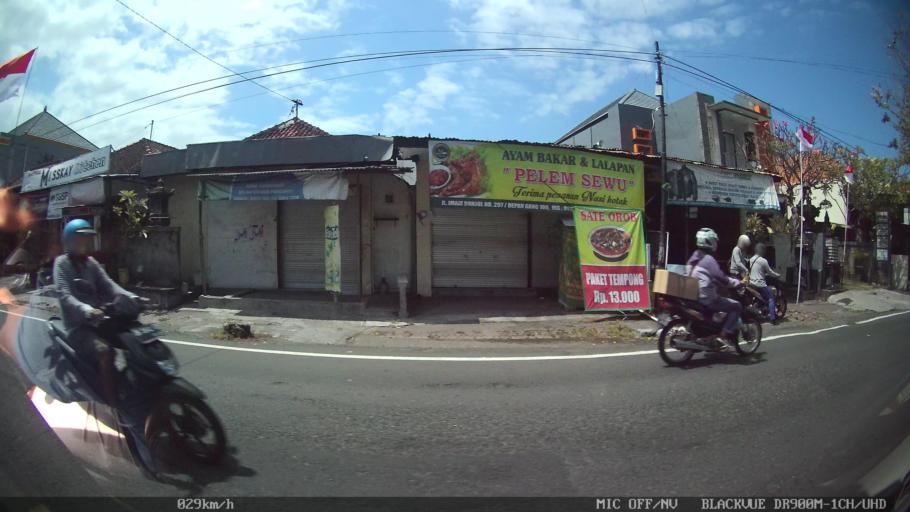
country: ID
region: Bali
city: Denpasar
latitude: -8.6717
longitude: 115.2042
